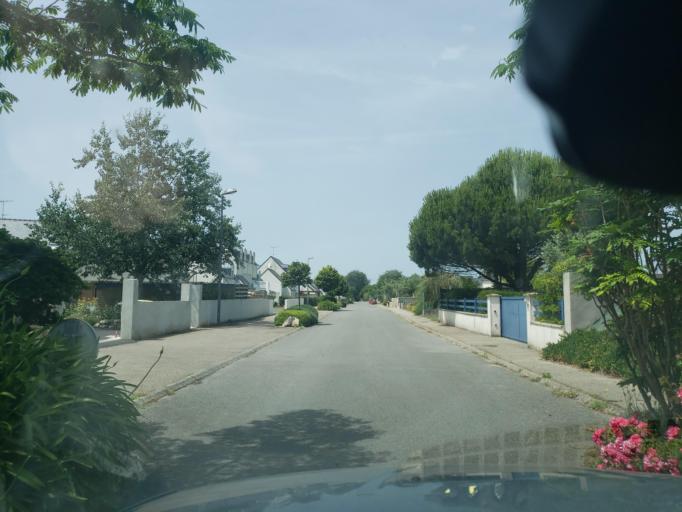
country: FR
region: Brittany
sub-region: Departement du Finistere
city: Guilvinec
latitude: 47.8015
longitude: -4.2908
